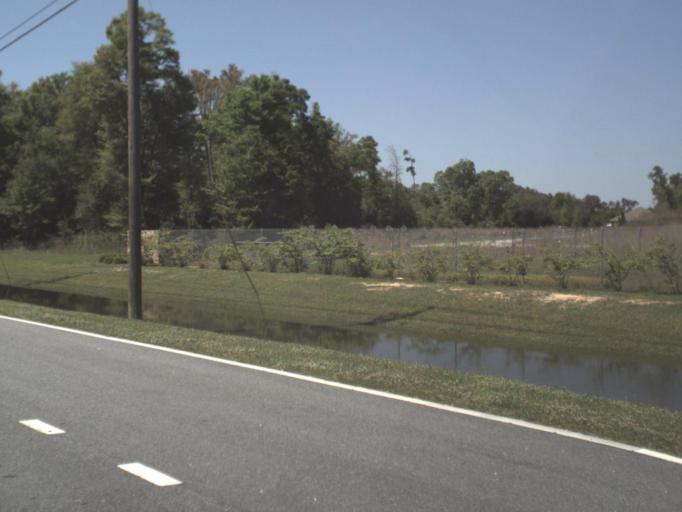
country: US
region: Florida
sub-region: Escambia County
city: Bellview
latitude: 30.5080
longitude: -87.3593
